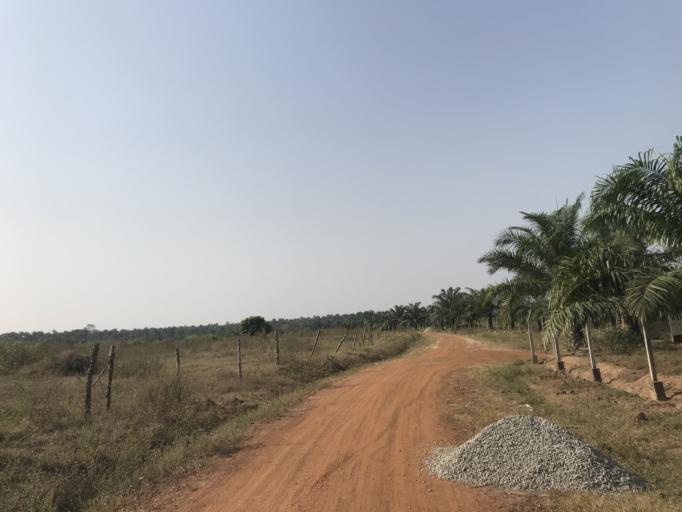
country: NG
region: Osun
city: Olupona
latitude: 7.5990
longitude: 4.1396
